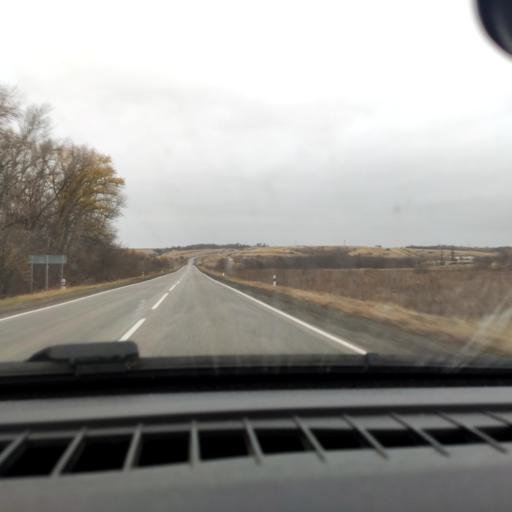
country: RU
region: Voronezj
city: Uryv-Pokrovka
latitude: 51.1270
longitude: 39.0405
